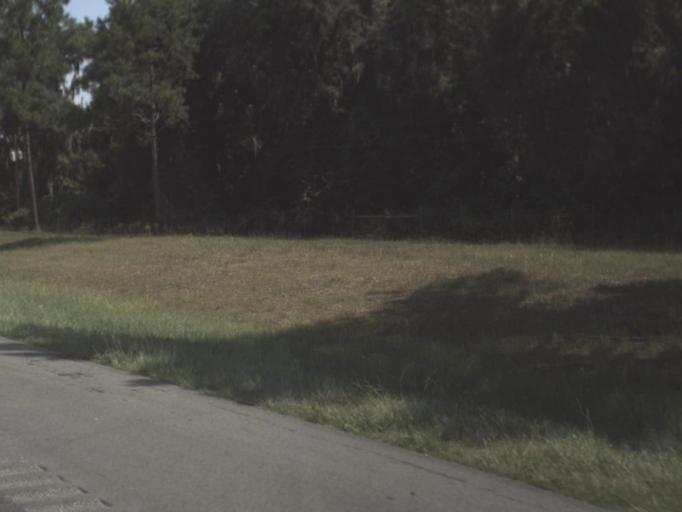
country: US
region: Florida
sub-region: Hamilton County
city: Jasper
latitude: 30.5481
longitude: -83.0777
